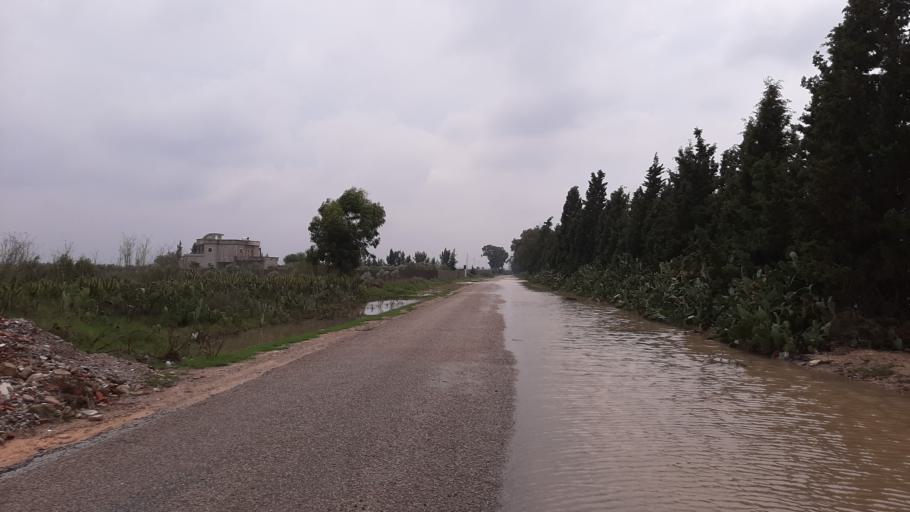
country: TN
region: Al Munastir
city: Sidi Bin Nur
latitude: 35.4547
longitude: 10.9044
